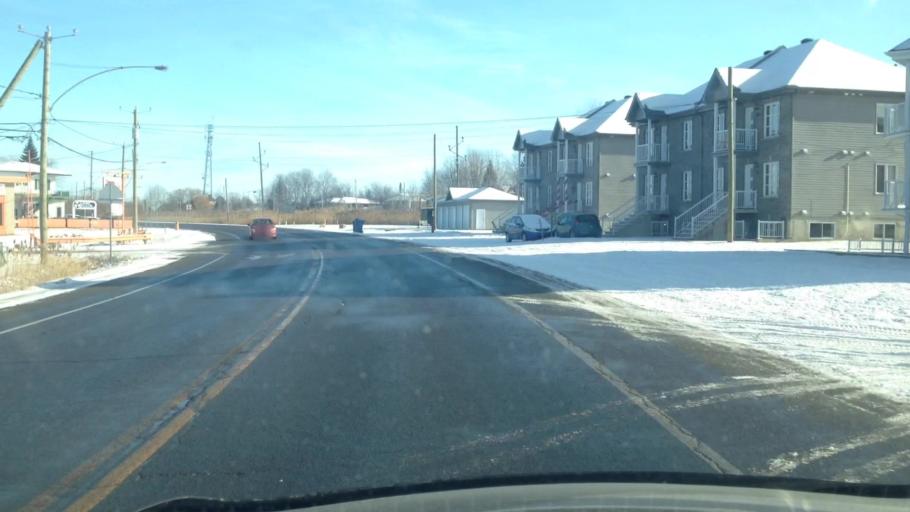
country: CA
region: Quebec
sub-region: Monteregie
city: Beauharnois
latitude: 45.3185
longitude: -73.8409
